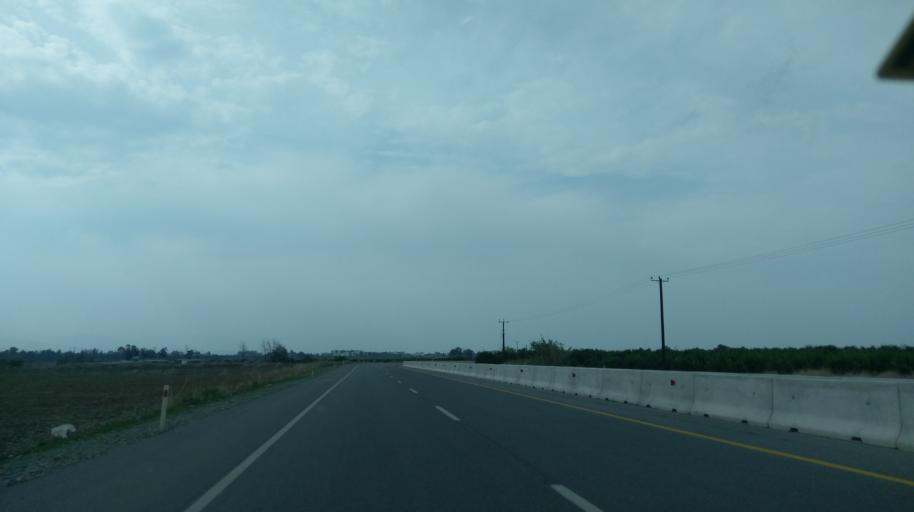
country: CY
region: Lefkosia
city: Morfou
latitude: 35.1991
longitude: 33.0243
